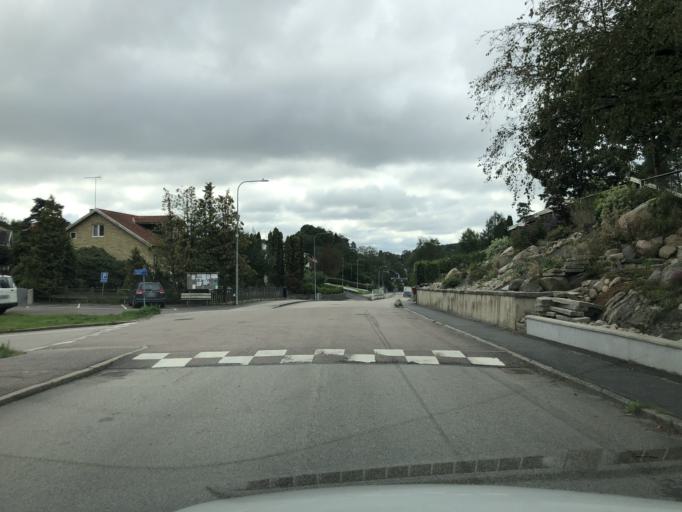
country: SE
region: Vaestra Goetaland
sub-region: Goteborg
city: Majorna
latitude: 57.7397
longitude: 11.9133
